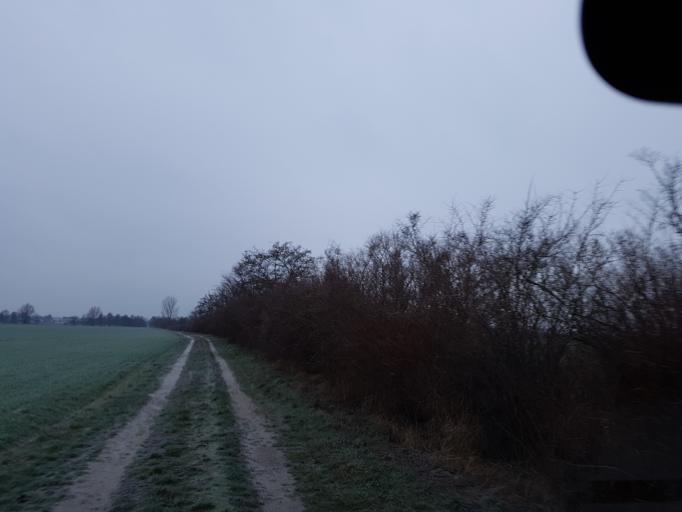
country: DE
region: Brandenburg
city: Ruckersdorf
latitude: 51.5735
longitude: 13.5536
